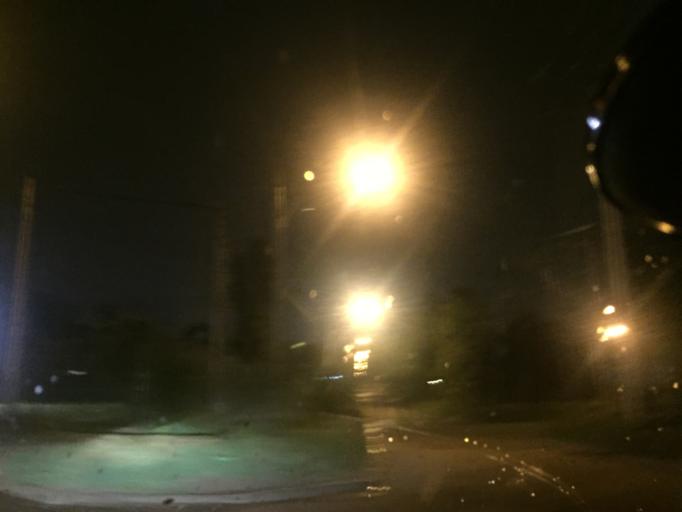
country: AR
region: Cordoba
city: Saldan
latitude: -31.3085
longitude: -64.2966
